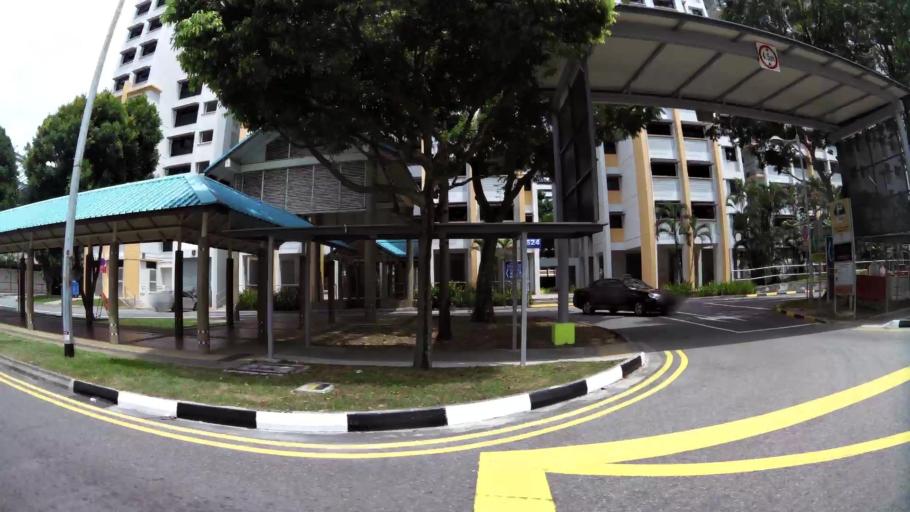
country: MY
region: Johor
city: Johor Bahru
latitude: 1.3405
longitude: 103.6976
